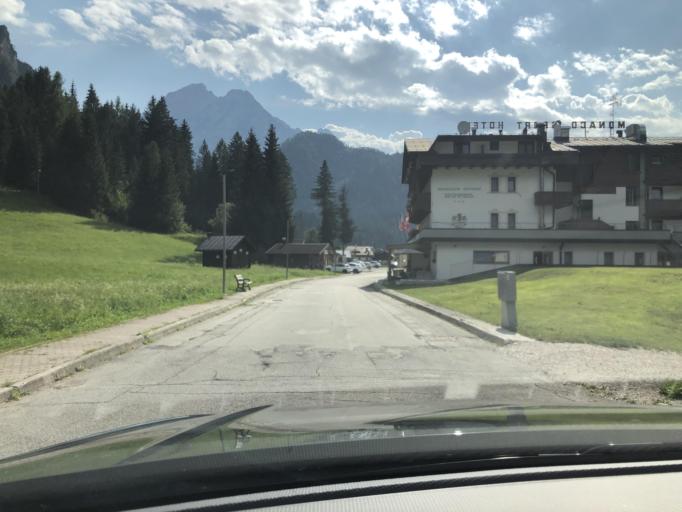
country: IT
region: Veneto
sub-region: Provincia di Belluno
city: Santo Stefano di Cadore
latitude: 46.5566
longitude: 12.5543
